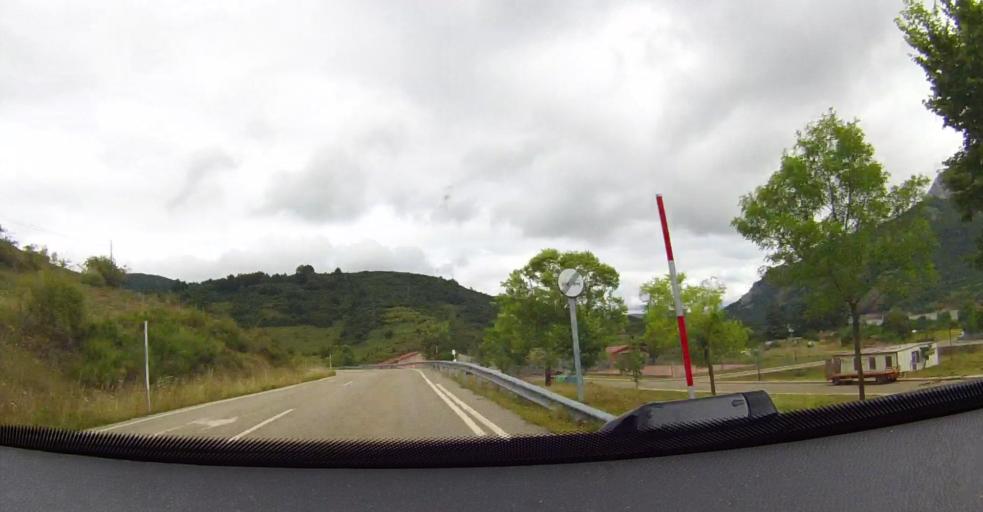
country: ES
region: Castille and Leon
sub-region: Provincia de Leon
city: Buron
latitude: 43.0261
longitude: -5.0503
